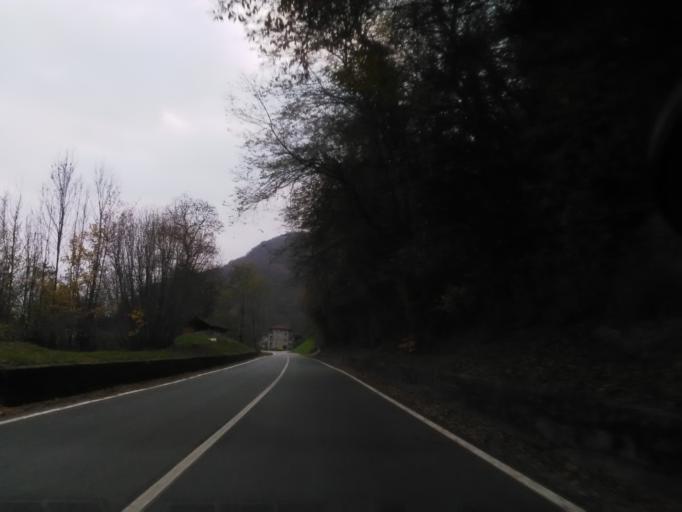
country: IT
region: Piedmont
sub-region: Provincia di Vercelli
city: Quarona
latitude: 45.7868
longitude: 8.2620
